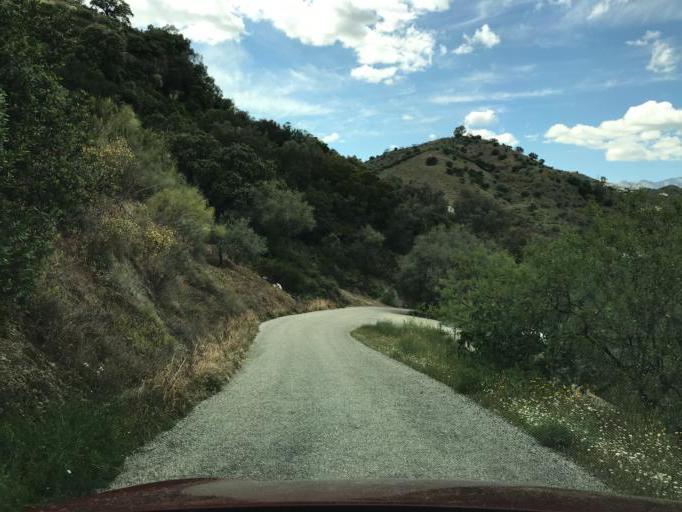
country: ES
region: Andalusia
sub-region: Provincia de Malaga
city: Comares
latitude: 36.8774
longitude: -4.2612
